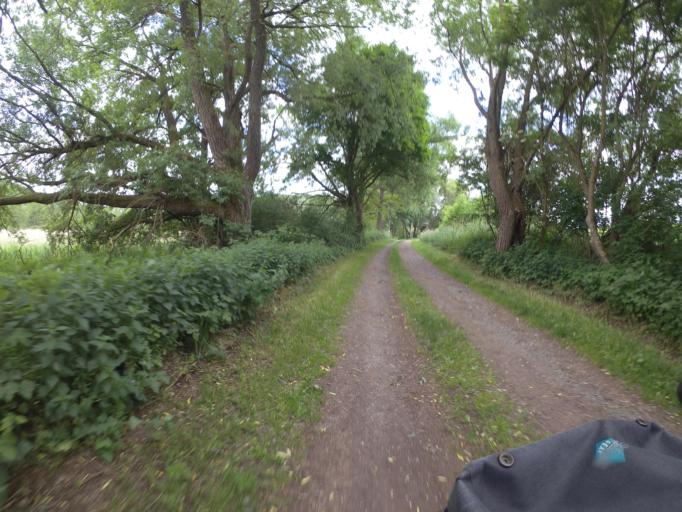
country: DE
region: Rheinland-Pfalz
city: Weilerbach
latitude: 49.4850
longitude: 7.6491
